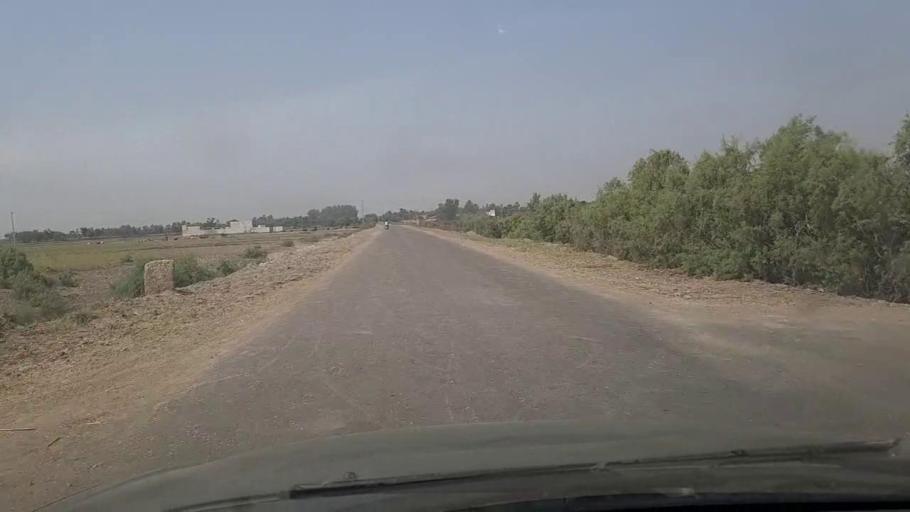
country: PK
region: Sindh
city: Khanpur
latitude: 27.8965
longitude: 69.4908
